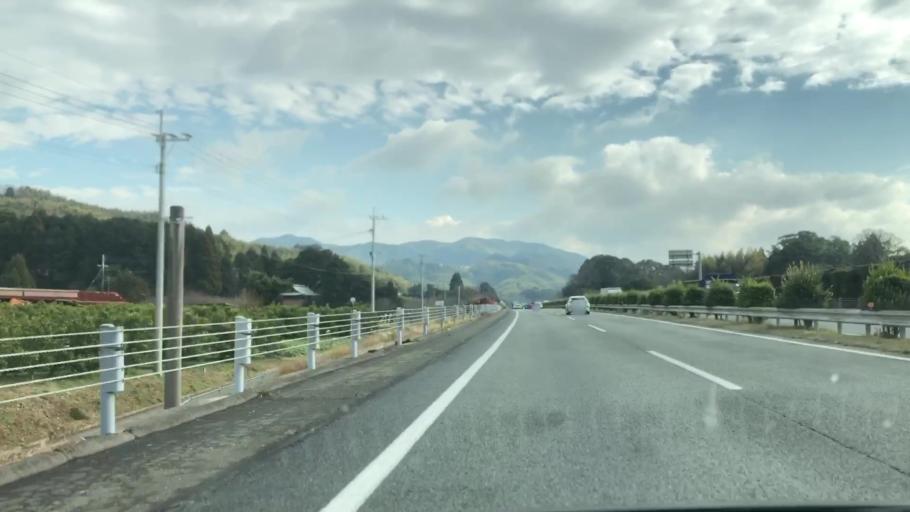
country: JP
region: Fukuoka
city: Setakamachi-takayanagi
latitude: 33.1197
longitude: 130.5228
